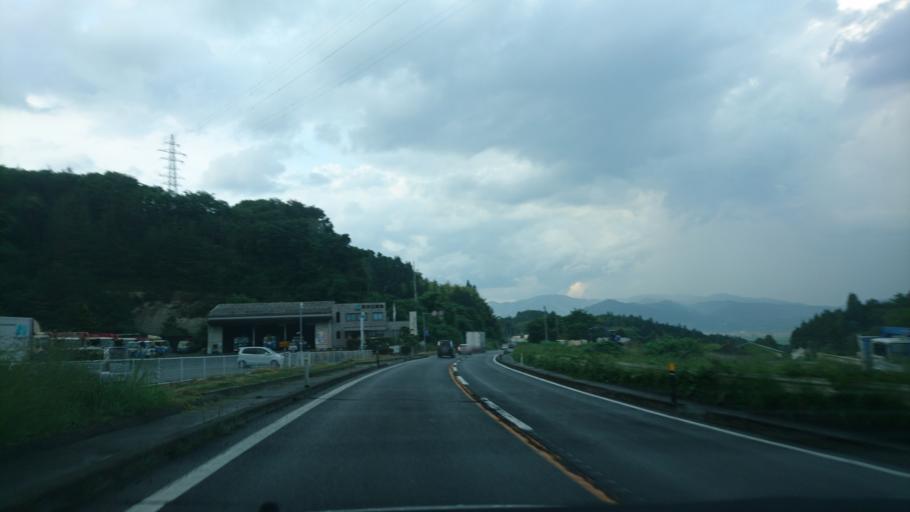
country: JP
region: Iwate
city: Ichinoseki
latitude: 38.9489
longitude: 141.1186
